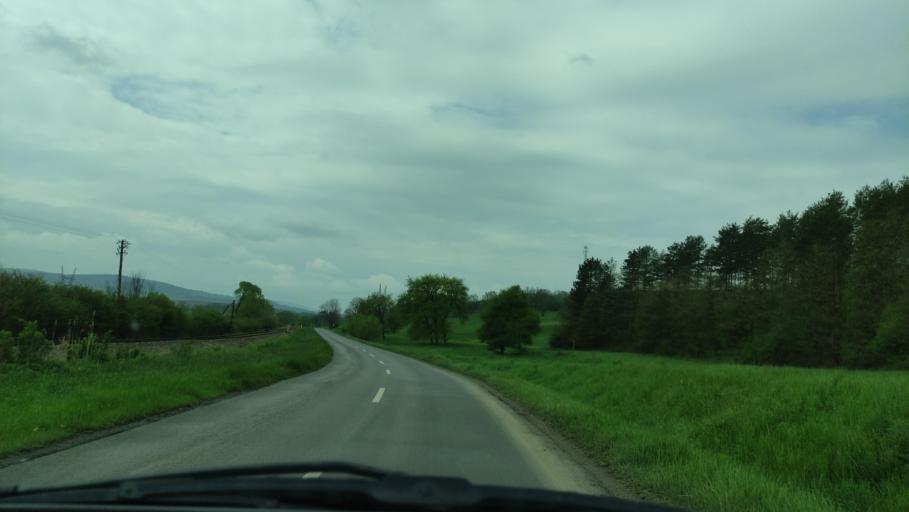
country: HU
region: Baranya
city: Komlo
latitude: 46.2198
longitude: 18.1969
